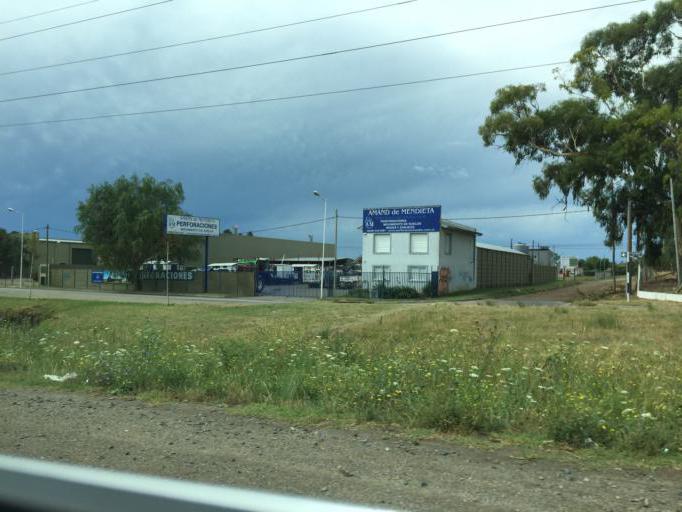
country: AR
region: Buenos Aires
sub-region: Partido de Tandil
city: Tandil
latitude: -37.3164
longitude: -59.1079
